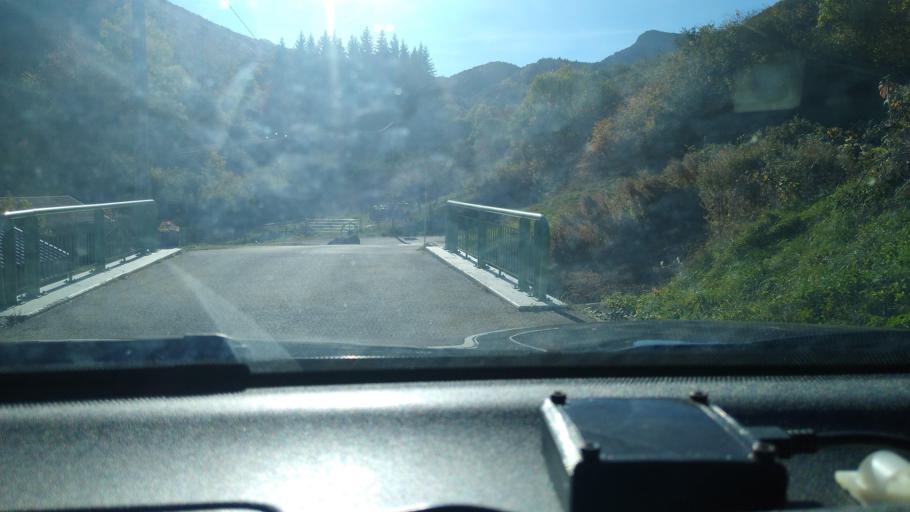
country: FR
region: Languedoc-Roussillon
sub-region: Departement de l'Aude
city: Quillan
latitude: 42.7297
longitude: 2.0545
